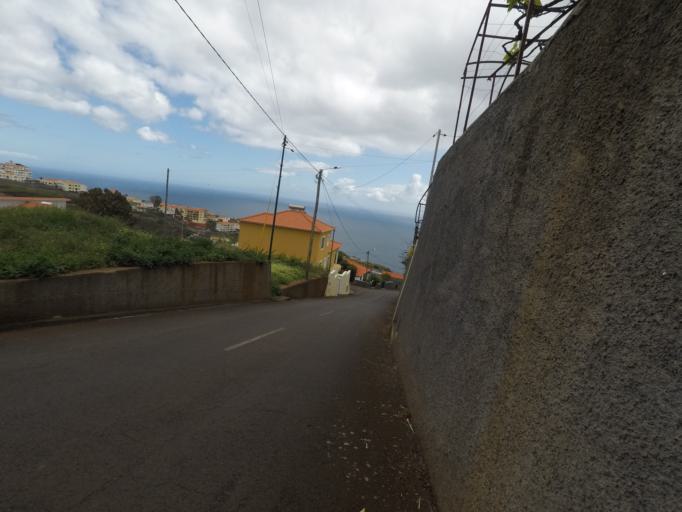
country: PT
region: Madeira
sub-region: Calheta
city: Estreito da Calheta
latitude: 32.7309
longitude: -17.1833
